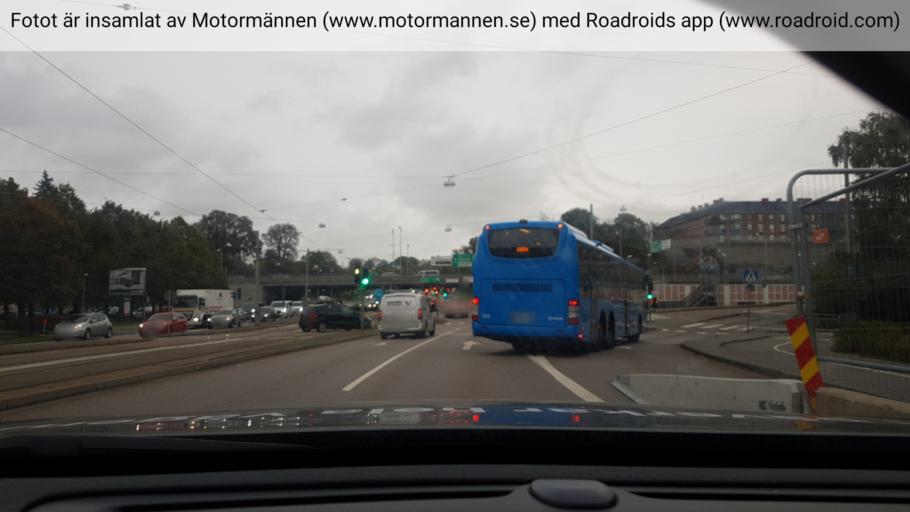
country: SE
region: Vaestra Goetaland
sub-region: Goteborg
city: Goeteborg
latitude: 57.6970
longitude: 11.9929
